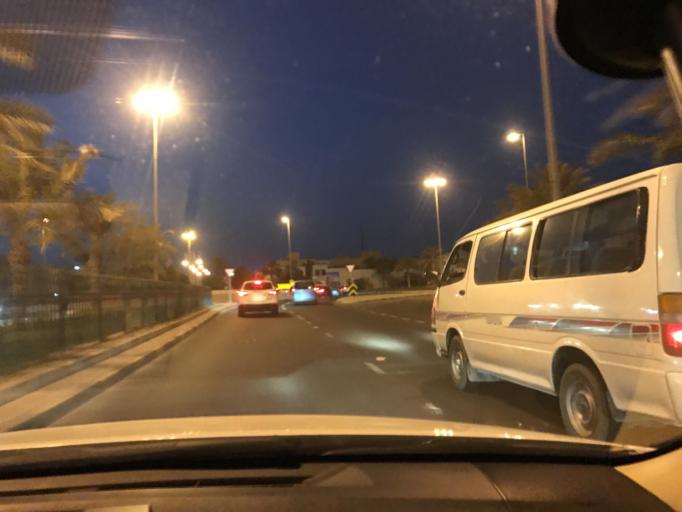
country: BH
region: Muharraq
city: Al Muharraq
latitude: 26.2657
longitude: 50.6034
